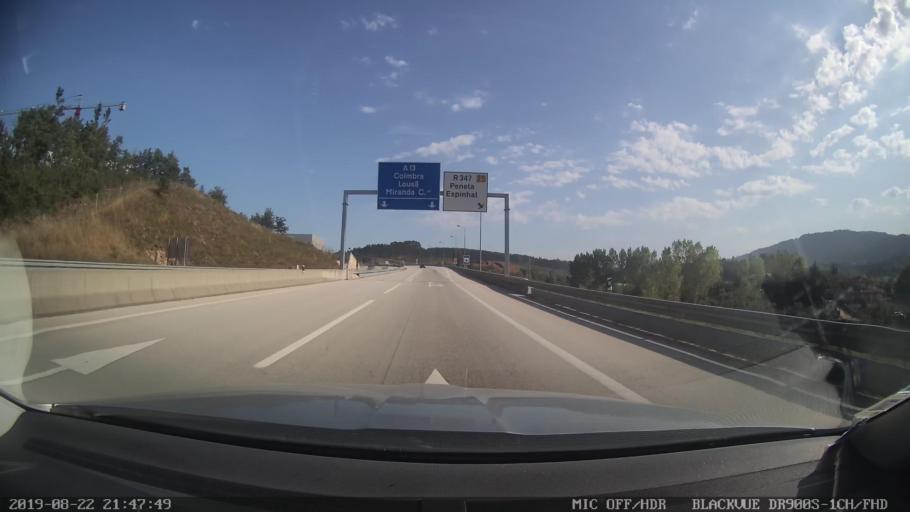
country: PT
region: Coimbra
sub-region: Penela
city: Penela
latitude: 40.0132
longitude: -8.3679
